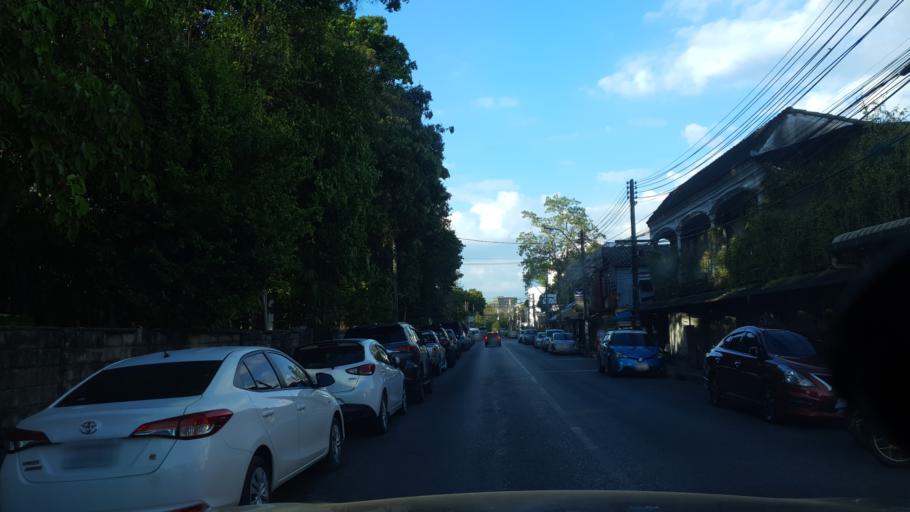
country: TH
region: Phuket
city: Ban Talat Nua
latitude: 7.8854
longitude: 98.3853
